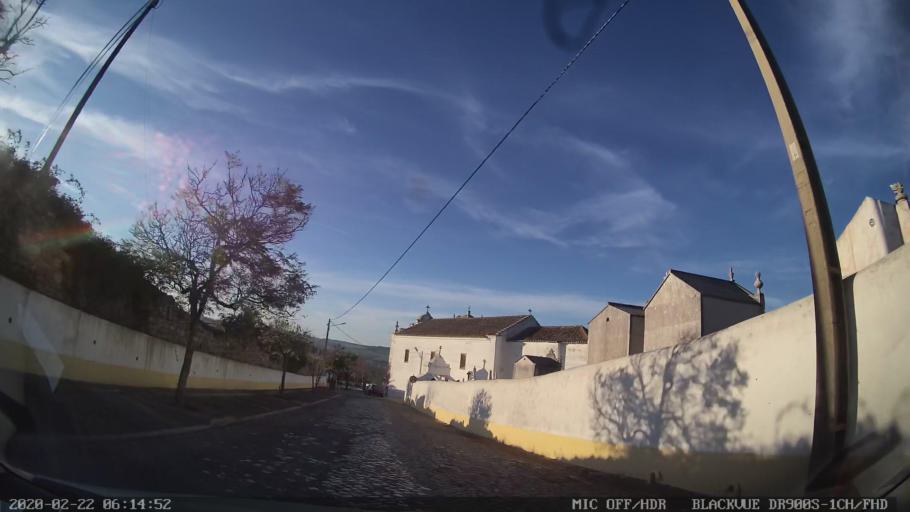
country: PT
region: Lisbon
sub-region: Vila Franca de Xira
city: Vila Franca de Xira
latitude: 38.9853
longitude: -9.0153
